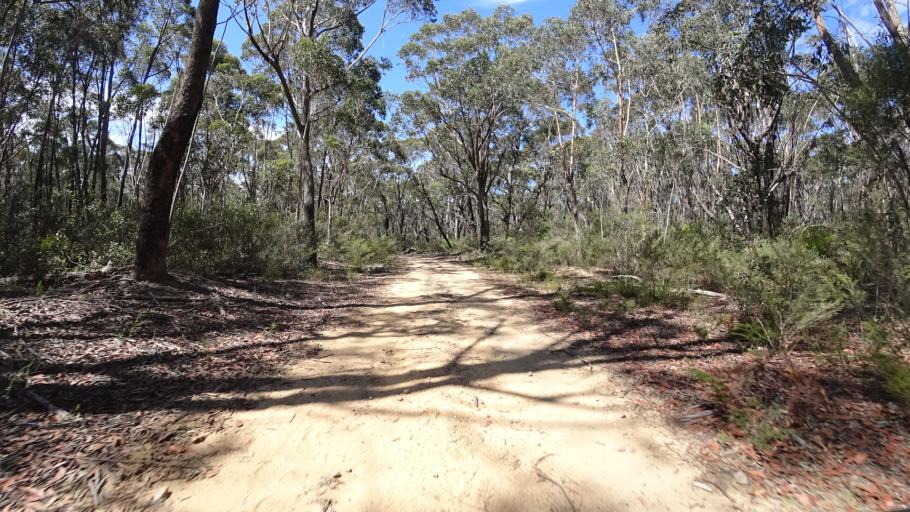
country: AU
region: New South Wales
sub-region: Lithgow
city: Lithgow
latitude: -33.3354
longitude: 150.2856
